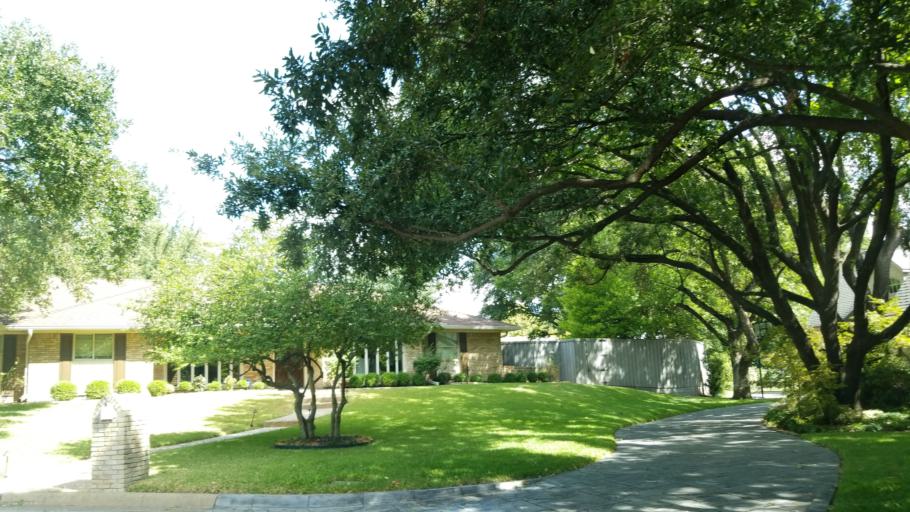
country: US
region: Texas
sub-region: Dallas County
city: Addison
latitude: 32.9320
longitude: -96.7994
